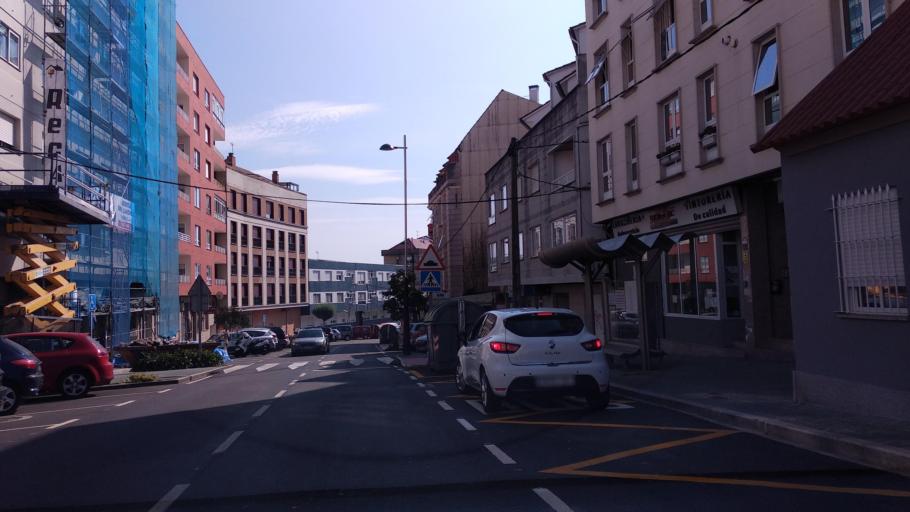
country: ES
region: Galicia
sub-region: Provincia de Pontevedra
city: Moana
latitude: 42.2758
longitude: -8.7393
